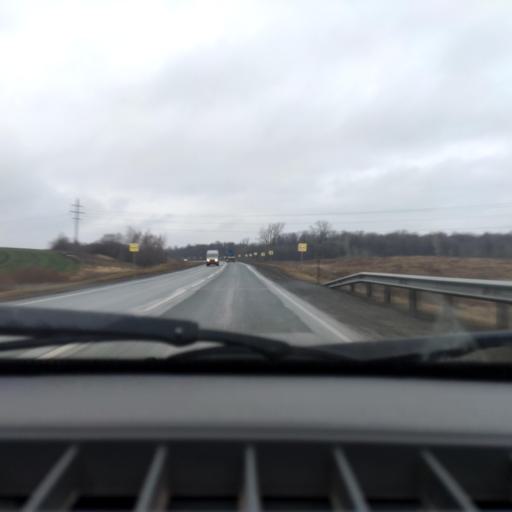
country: RU
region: Bashkortostan
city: Avdon
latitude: 54.7335
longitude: 55.7815
